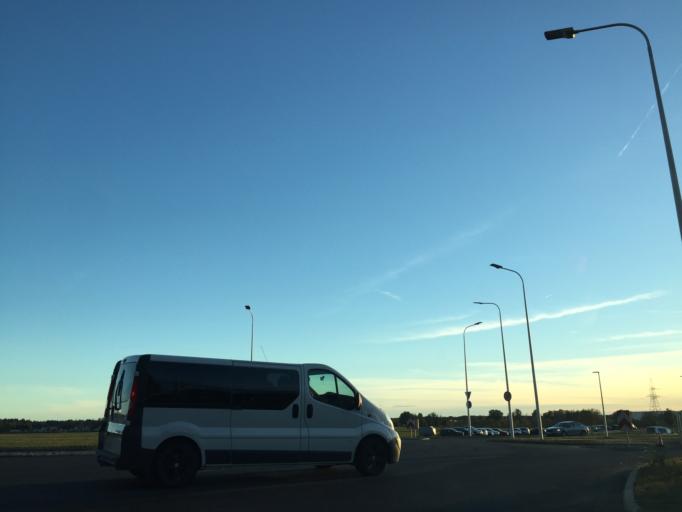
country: LV
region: Stopini
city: Ulbroka
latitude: 56.9530
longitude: 24.2578
